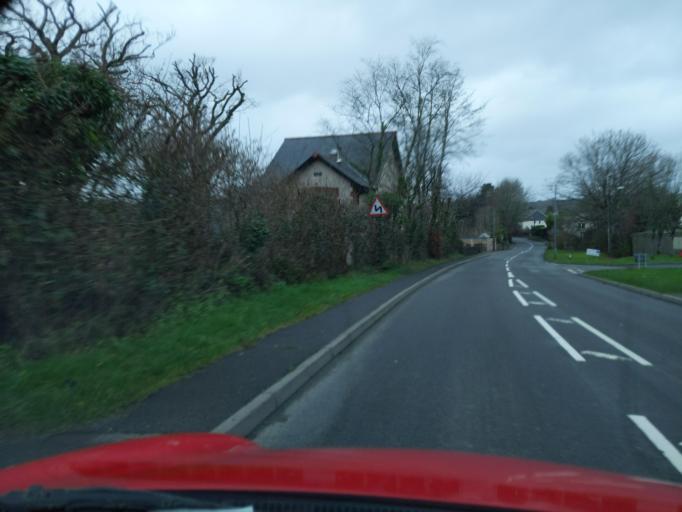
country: GB
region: England
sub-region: Devon
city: Holsworthy
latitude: 50.7670
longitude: -4.3364
